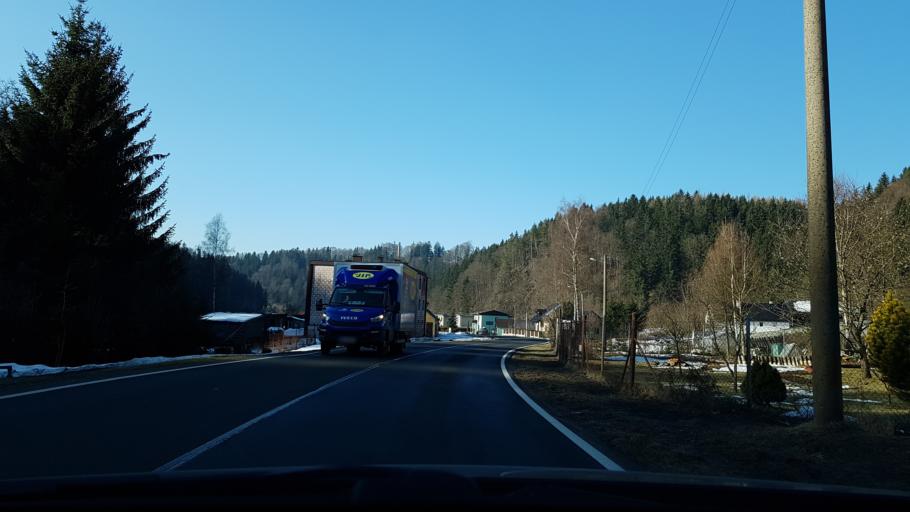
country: CZ
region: Olomoucky
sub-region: Okres Sumperk
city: Hanusovice
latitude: 50.1113
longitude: 17.0033
